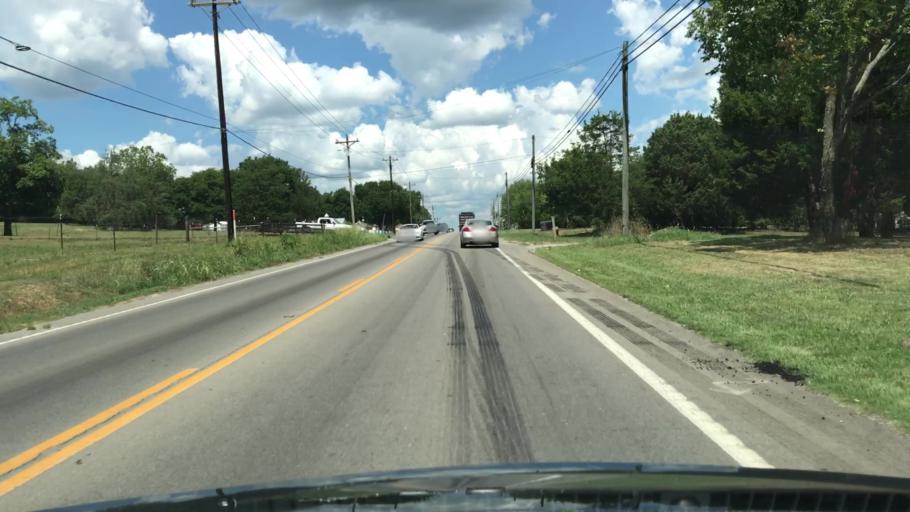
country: US
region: Tennessee
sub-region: Williamson County
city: Nolensville
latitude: 35.9444
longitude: -86.6648
